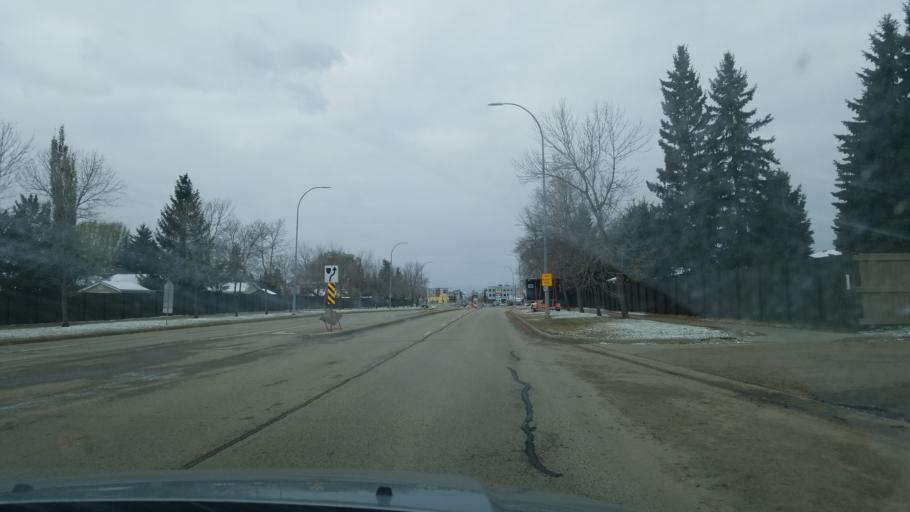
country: CA
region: Alberta
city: Sherwood Park
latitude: 53.5288
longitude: -113.2850
